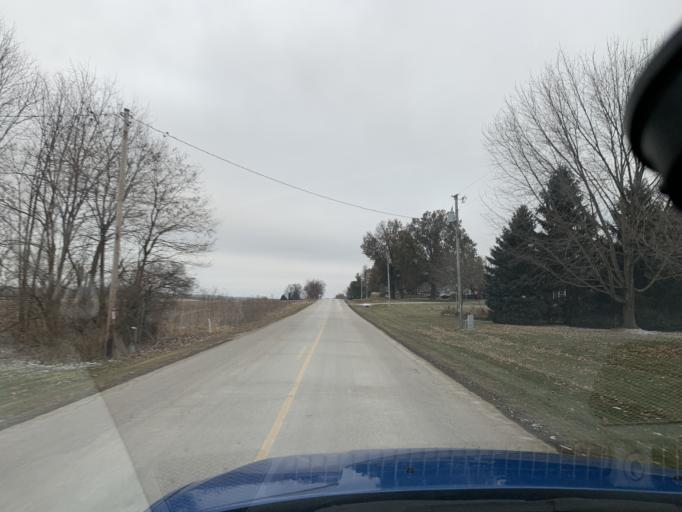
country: US
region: Wisconsin
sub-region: Dane County
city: Middleton
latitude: 43.0642
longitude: -89.5716
